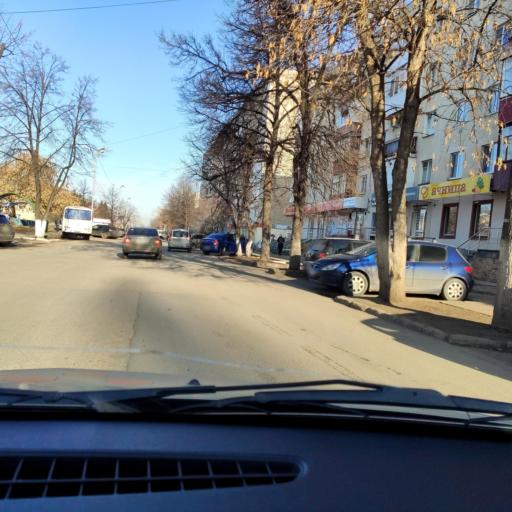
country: RU
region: Bashkortostan
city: Mikhaylovka
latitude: 54.7077
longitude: 55.8284
